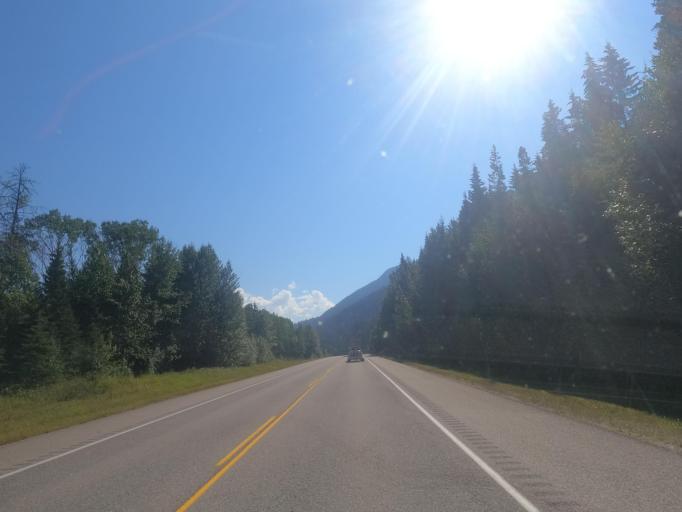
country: CA
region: Alberta
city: Jasper Park Lodge
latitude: 52.8589
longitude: -118.1708
